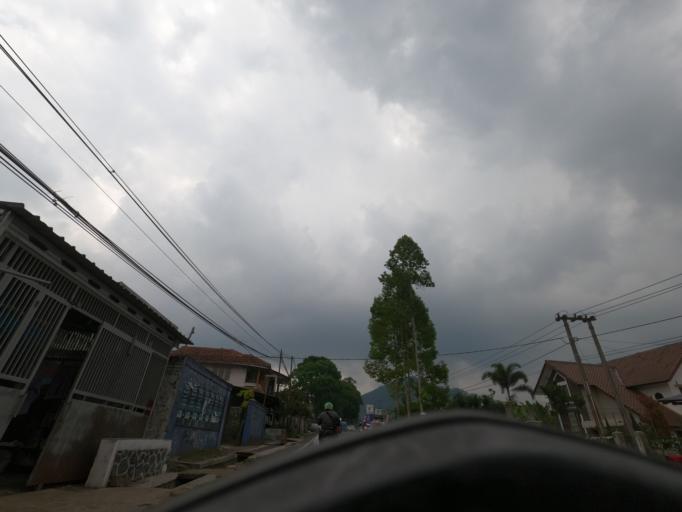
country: ID
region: West Java
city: Sukabumi
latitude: -6.7754
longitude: 107.0637
